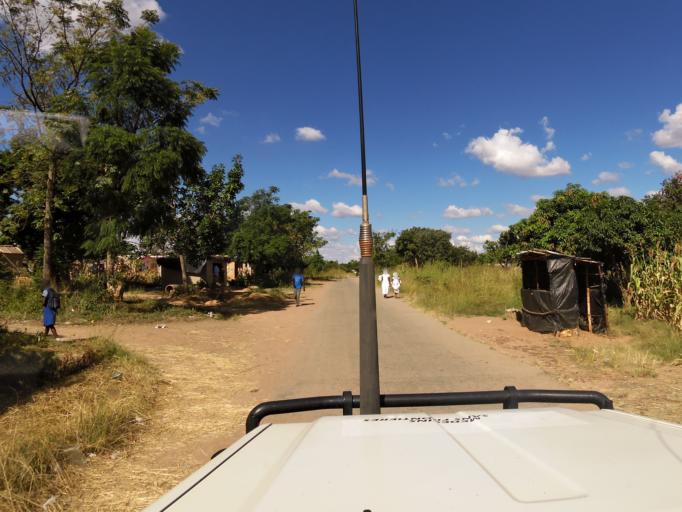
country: ZW
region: Harare
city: Epworth
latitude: -17.8713
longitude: 31.1381
